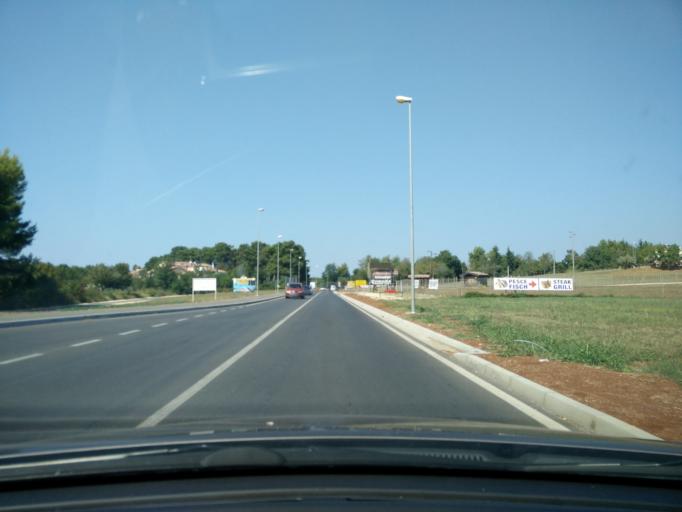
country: HR
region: Istarska
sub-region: Grad Porec
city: Porec
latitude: 45.2078
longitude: 13.6033
